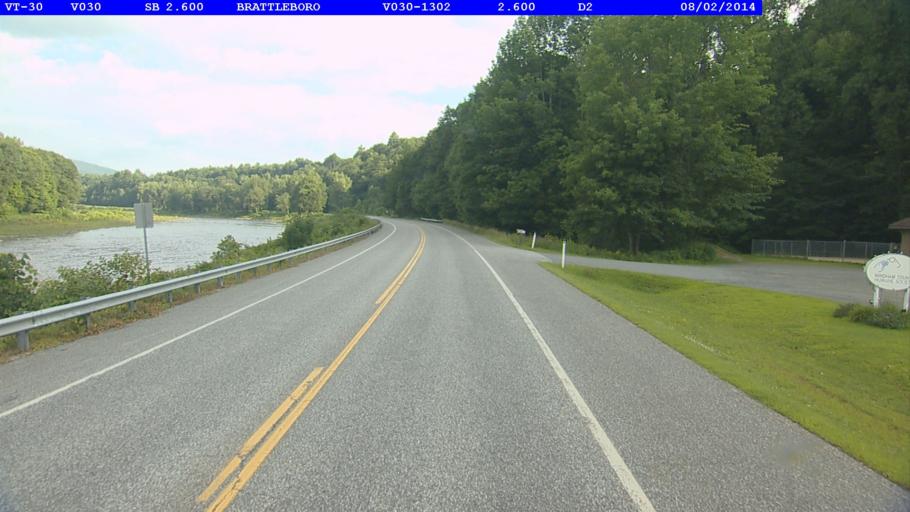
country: US
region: Vermont
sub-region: Windham County
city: West Brattleboro
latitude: 42.8860
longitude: -72.5891
